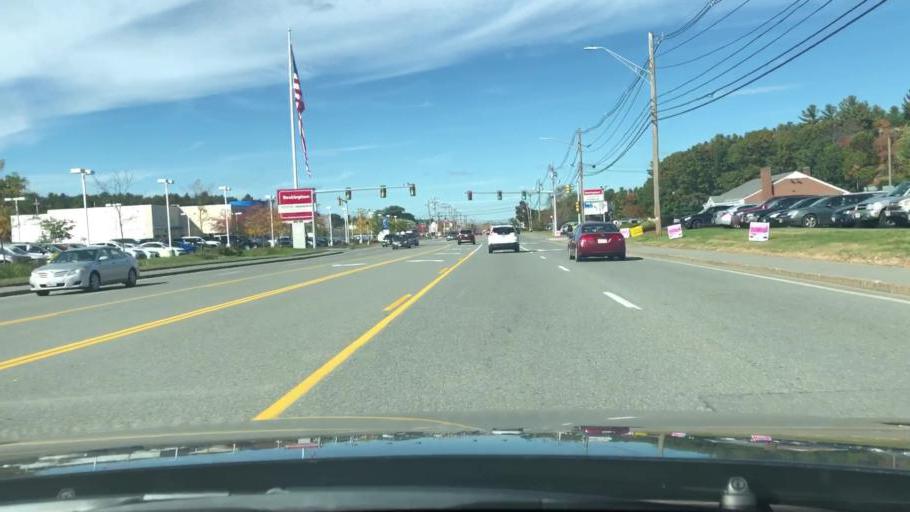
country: US
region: Massachusetts
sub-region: Essex County
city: Methuen
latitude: 42.7483
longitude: -71.2034
